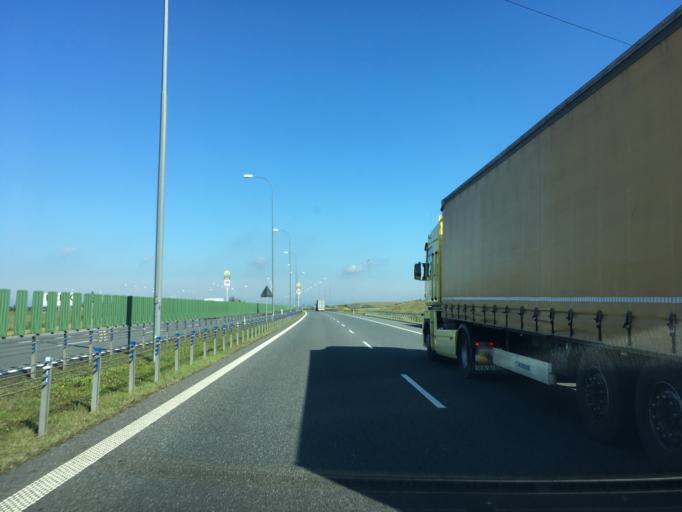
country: PL
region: Kujawsko-Pomorskie
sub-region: Powiat chelminski
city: Lisewo
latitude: 53.3368
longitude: 18.7093
